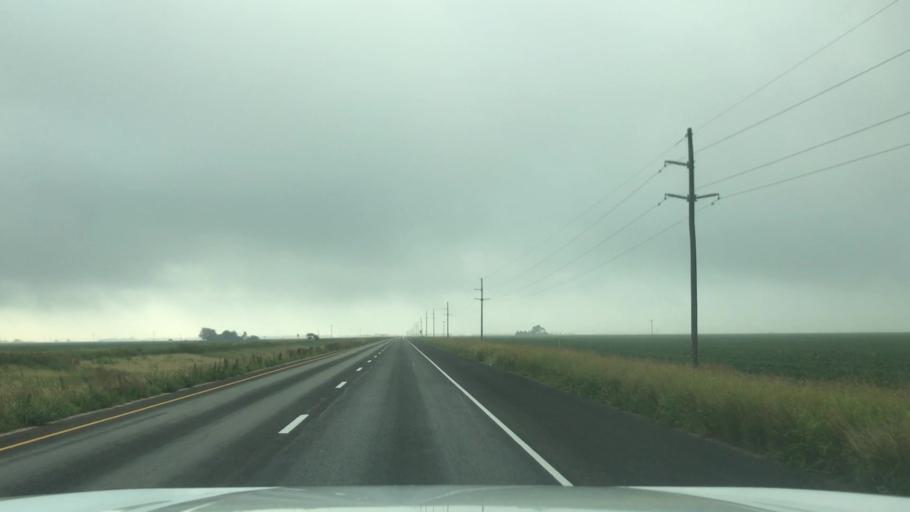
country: US
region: Texas
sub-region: Lubbock County
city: Slaton
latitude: 33.3777
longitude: -101.5816
